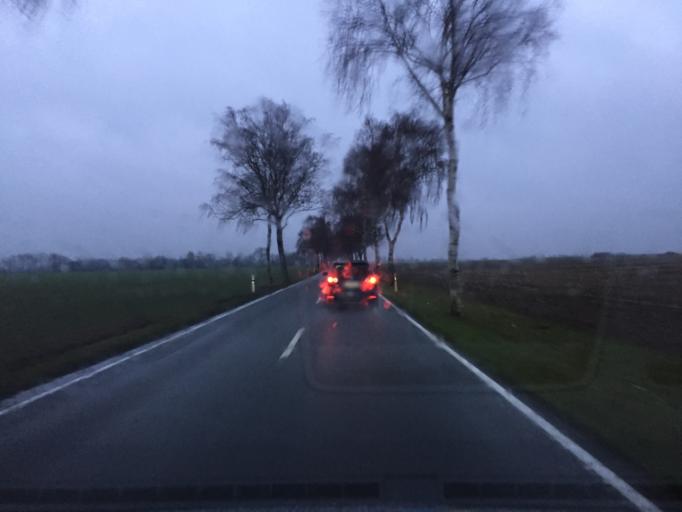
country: DE
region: Lower Saxony
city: Sustedt
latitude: 52.8672
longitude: 8.8599
